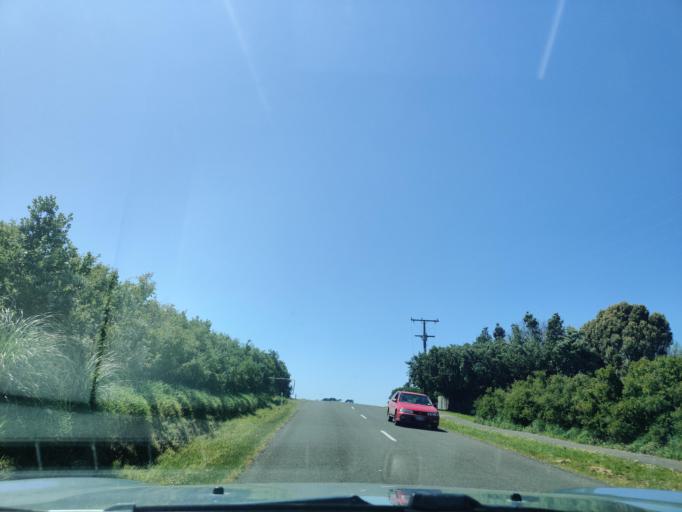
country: NZ
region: Taranaki
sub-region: South Taranaki District
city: Hawera
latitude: -39.6014
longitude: 174.2494
